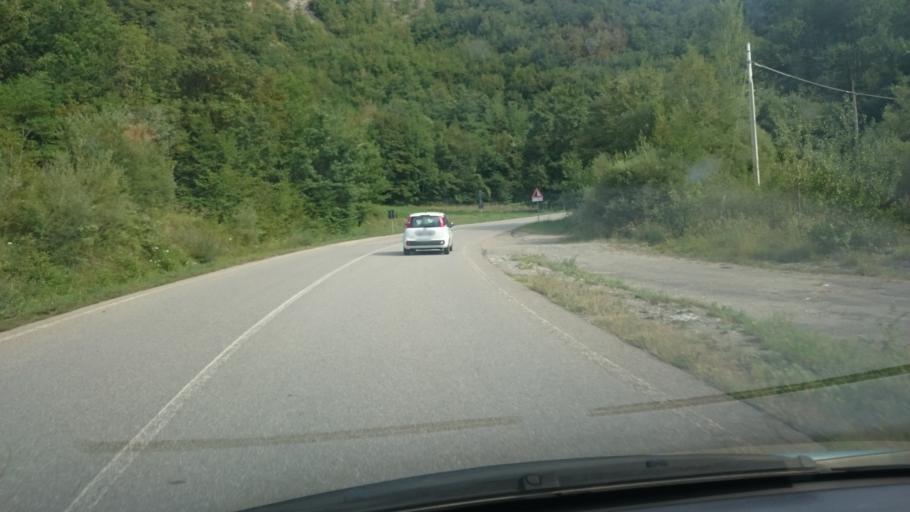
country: IT
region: Emilia-Romagna
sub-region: Provincia di Reggio Emilia
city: Villa Minozzo
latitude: 44.3164
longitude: 10.4639
